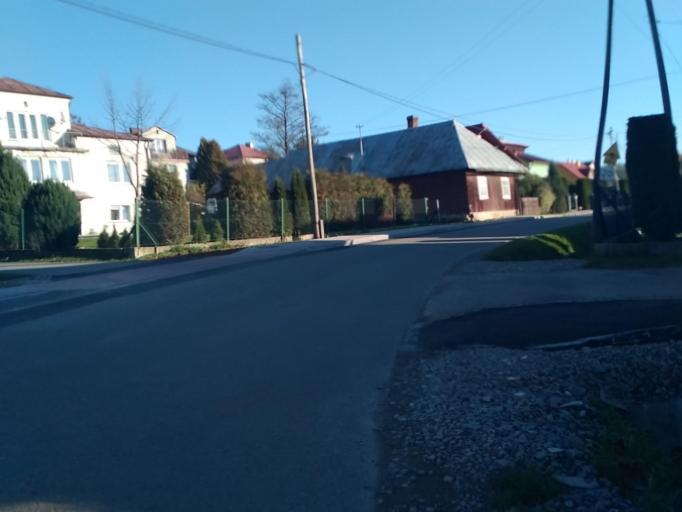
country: PL
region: Subcarpathian Voivodeship
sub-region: Powiat brzozowski
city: Brzozow
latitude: 49.7005
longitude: 22.0285
